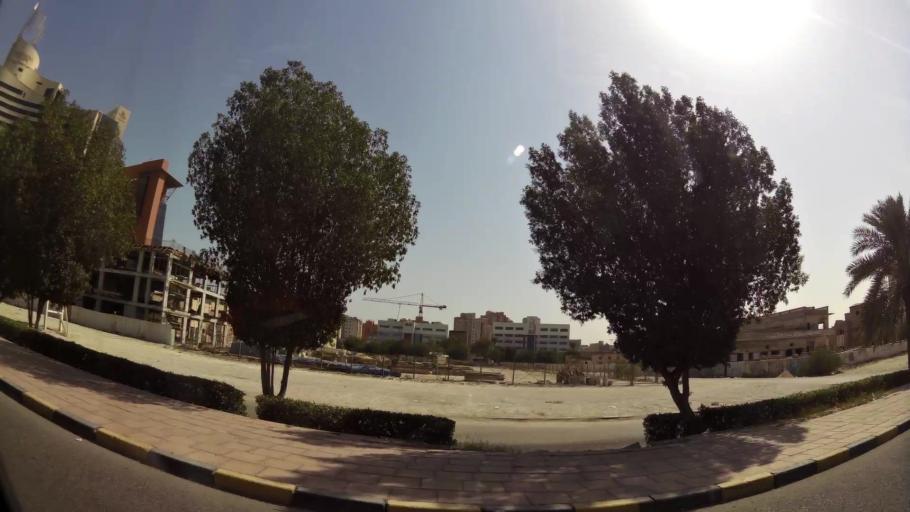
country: KW
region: Muhafazat Hawalli
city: As Salimiyah
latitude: 29.3465
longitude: 48.0827
